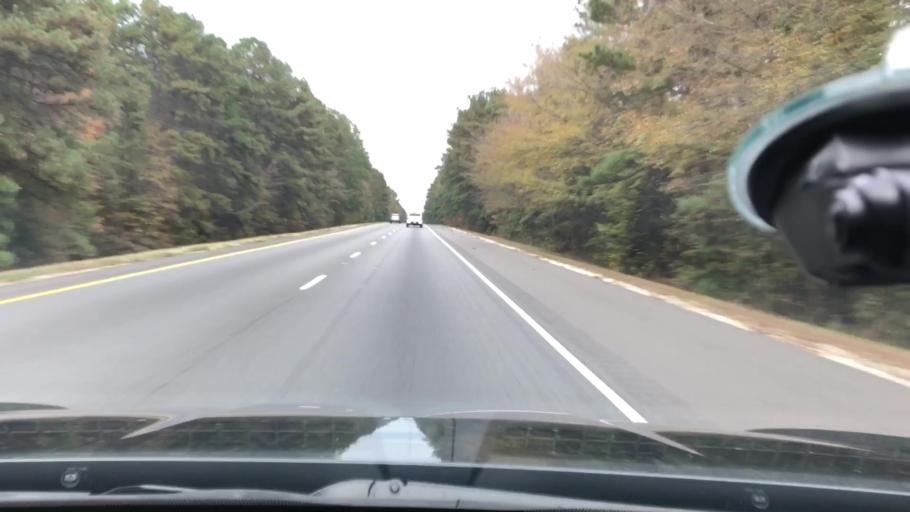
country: US
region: Arkansas
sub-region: Hot Spring County
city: Malvern
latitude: 34.2931
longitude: -92.9505
